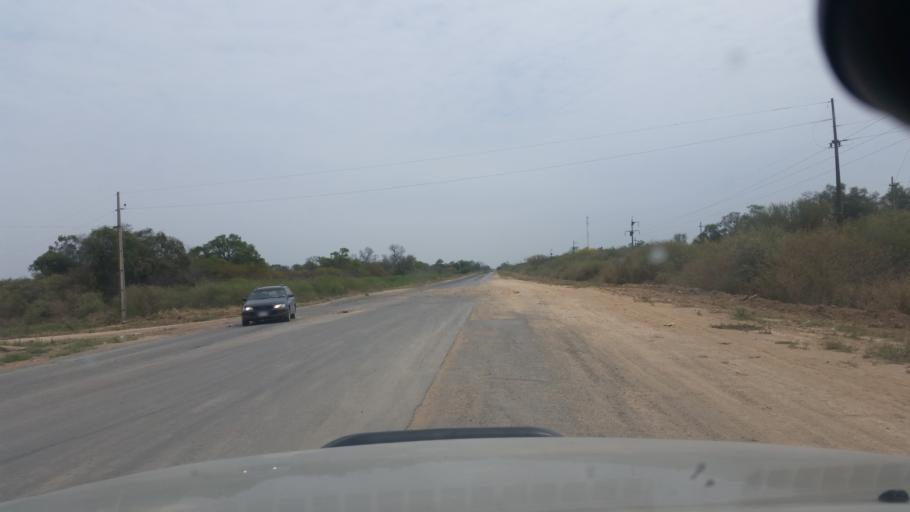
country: PY
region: Boqueron
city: Filadelfia
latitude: -22.2340
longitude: -60.3983
